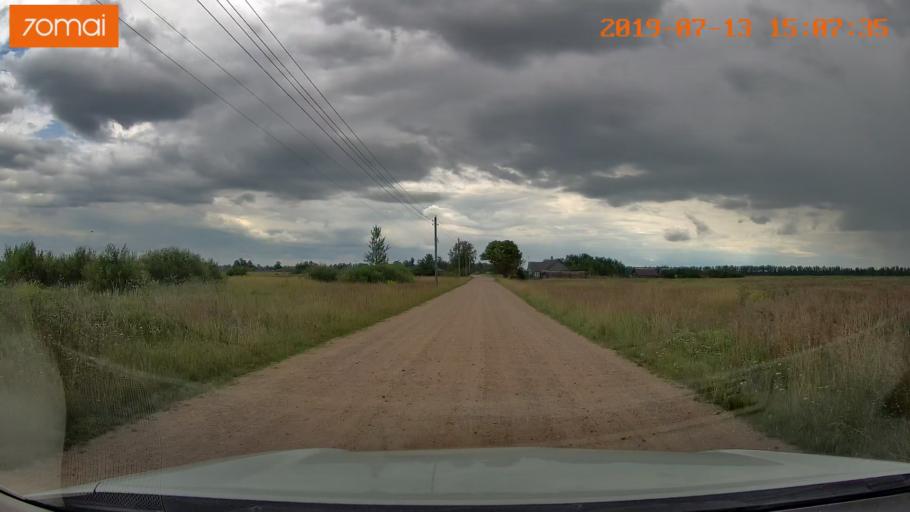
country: BY
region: Mogilev
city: Hlusha
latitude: 53.1889
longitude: 28.7569
